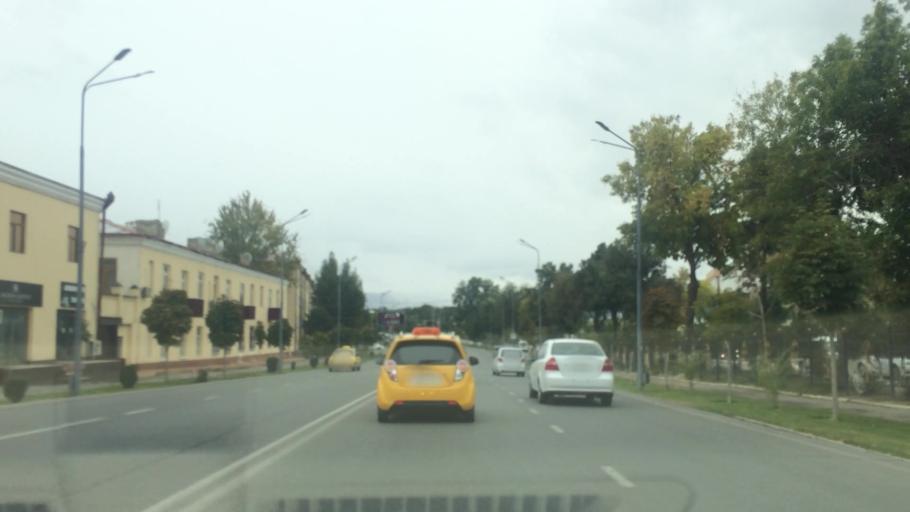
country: UZ
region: Samarqand
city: Samarqand
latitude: 39.6548
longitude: 66.9709
